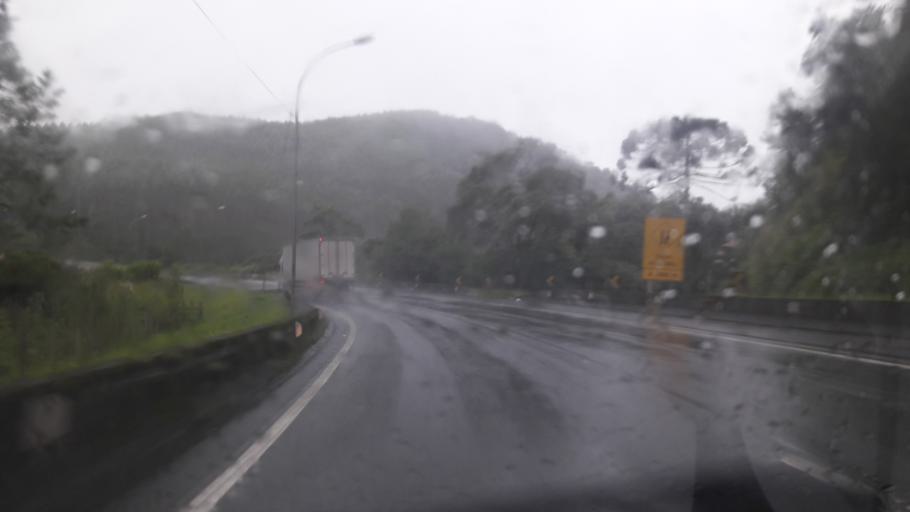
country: BR
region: Parana
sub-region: Campina Grande Do Sul
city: Campina Grande do Sul
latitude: -25.1127
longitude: -48.8040
